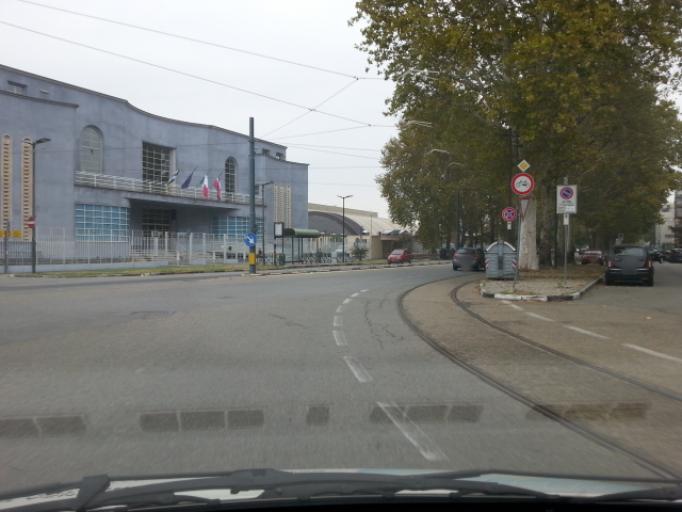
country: IT
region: Piedmont
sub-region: Provincia di Torino
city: Lesna
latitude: 45.0392
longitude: 7.6530
